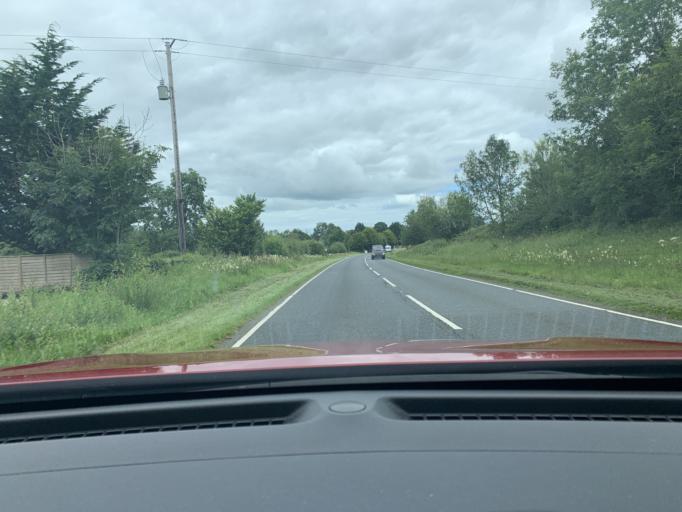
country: GB
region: Northern Ireland
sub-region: Fermanagh District
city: Enniskillen
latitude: 54.3228
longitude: -7.6796
